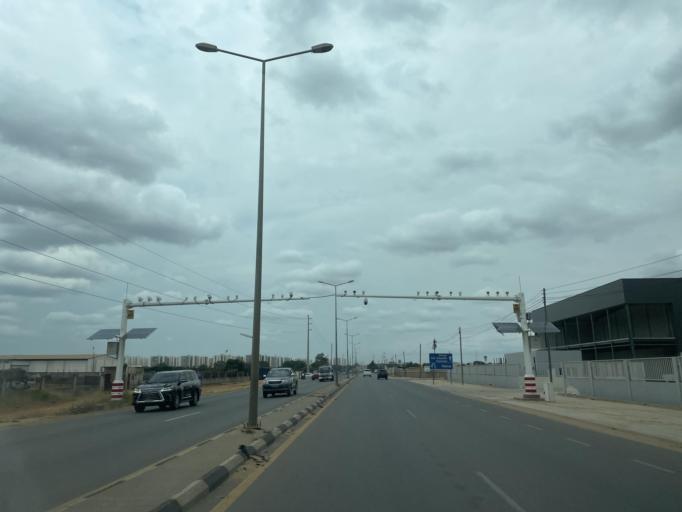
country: AO
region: Luanda
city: Luanda
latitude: -8.9672
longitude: 13.3904
